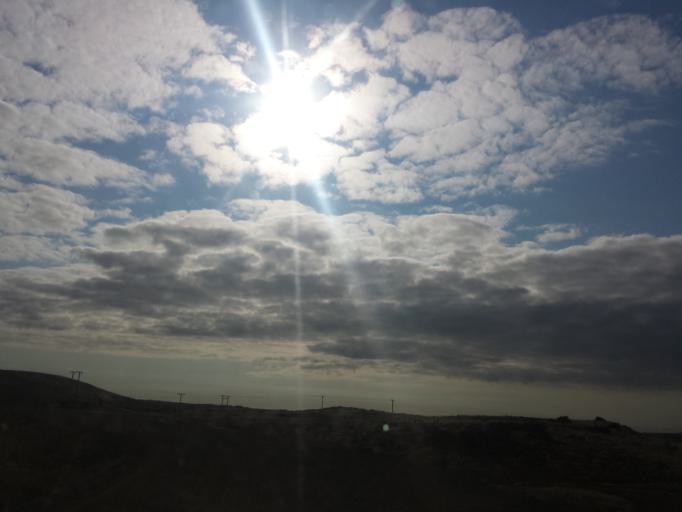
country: IS
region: Capital Region
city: Mosfellsbaer
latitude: 64.0754
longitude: -21.6494
